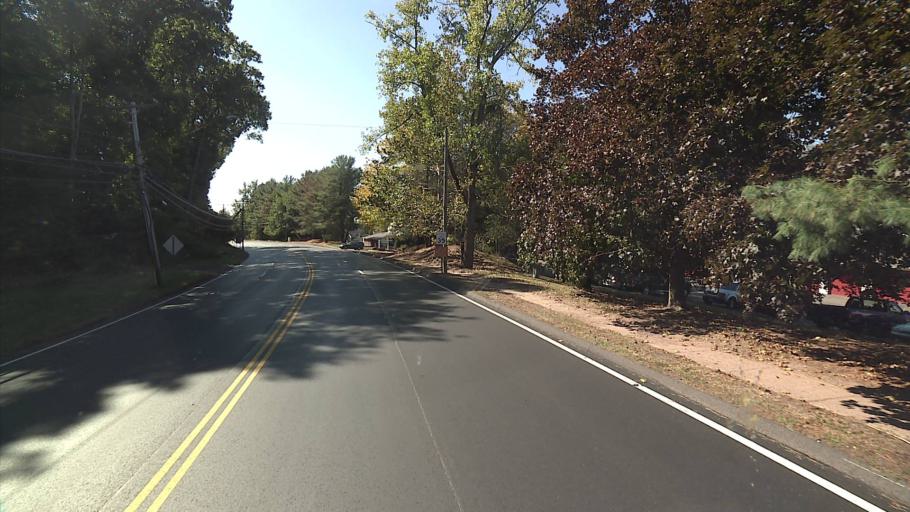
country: US
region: Connecticut
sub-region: Tolland County
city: Rockville
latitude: 41.8591
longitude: -72.4847
